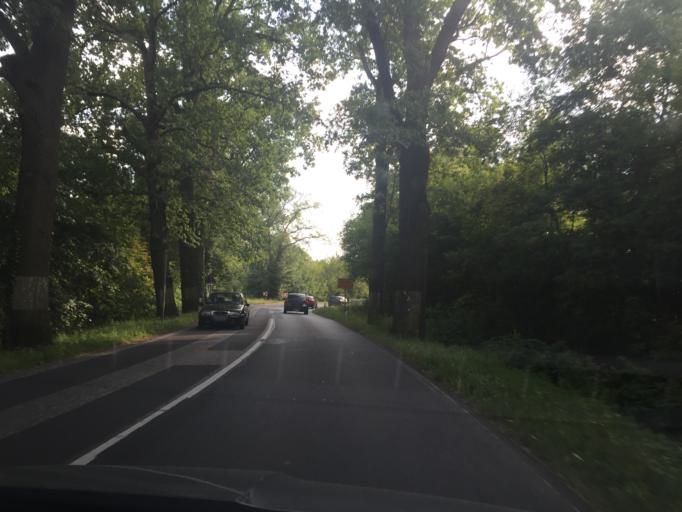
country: DE
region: Brandenburg
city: Erkner
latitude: 52.3935
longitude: 13.7451
